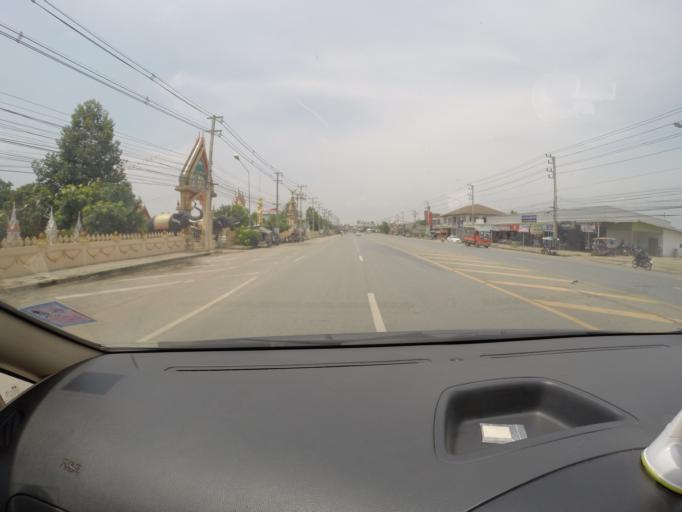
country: TH
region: Chaiyaphum
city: Noen Sa-nga
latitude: 15.6864
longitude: 102.0105
